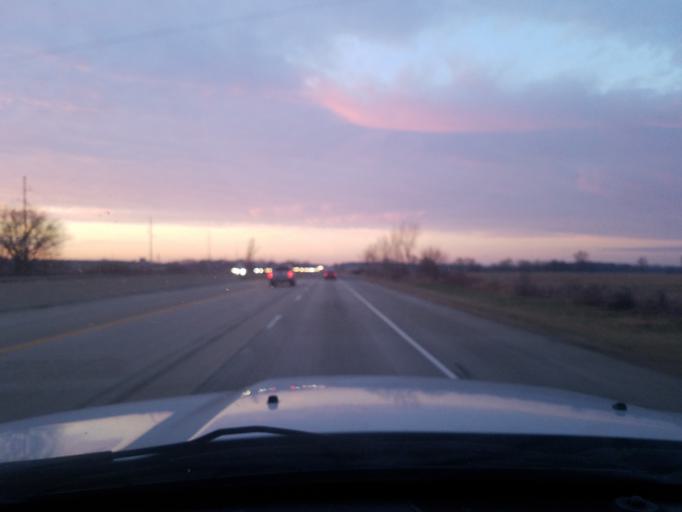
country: US
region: Indiana
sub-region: Huntington County
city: Roanoke
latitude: 41.0158
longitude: -85.2546
